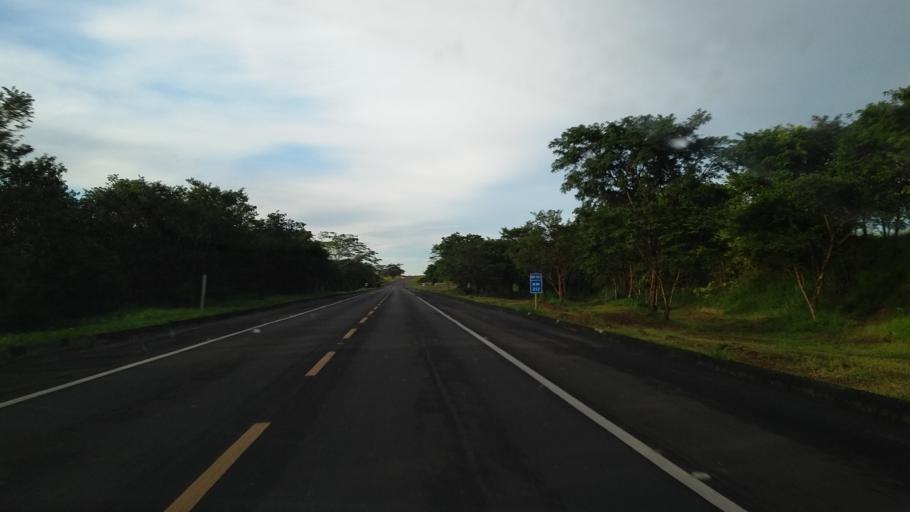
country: BR
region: Sao Paulo
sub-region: Marilia
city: Marilia
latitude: -21.9240
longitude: -49.9172
